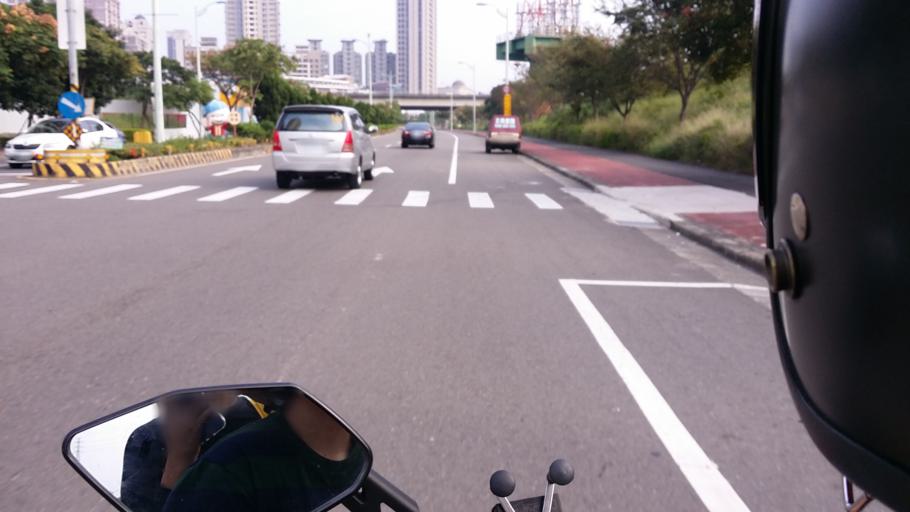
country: TW
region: Taiwan
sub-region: Hsinchu
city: Zhubei
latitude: 24.8179
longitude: 121.0111
